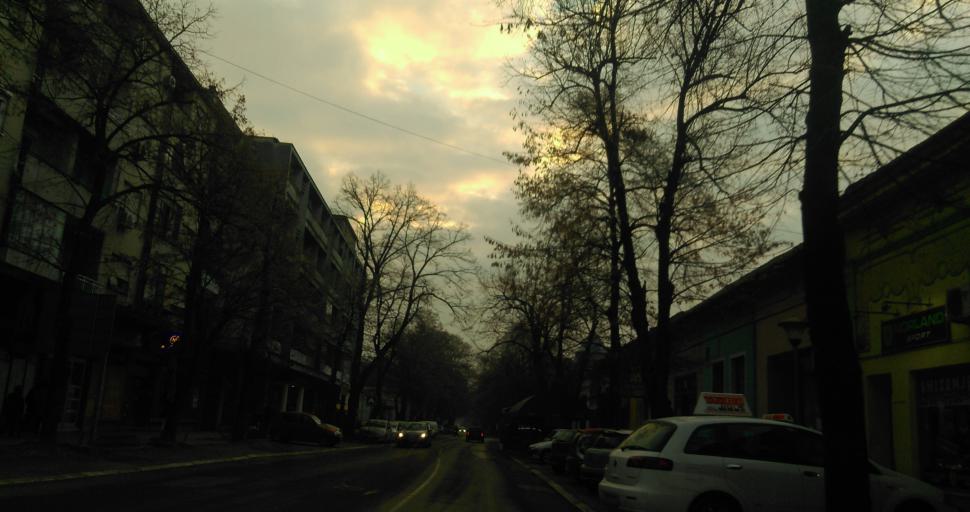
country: RS
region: Autonomna Pokrajina Vojvodina
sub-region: Juznobacki Okrug
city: Becej
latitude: 45.6143
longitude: 20.0476
